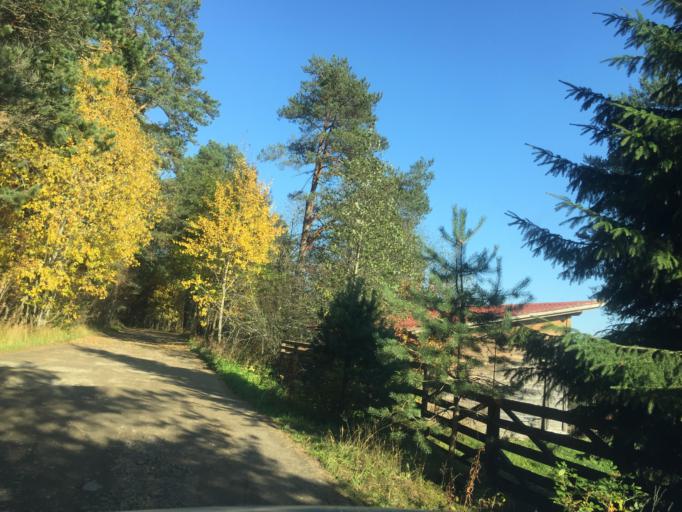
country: RU
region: Leningrad
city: Kuznechnoye
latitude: 61.2951
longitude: 30.0594
